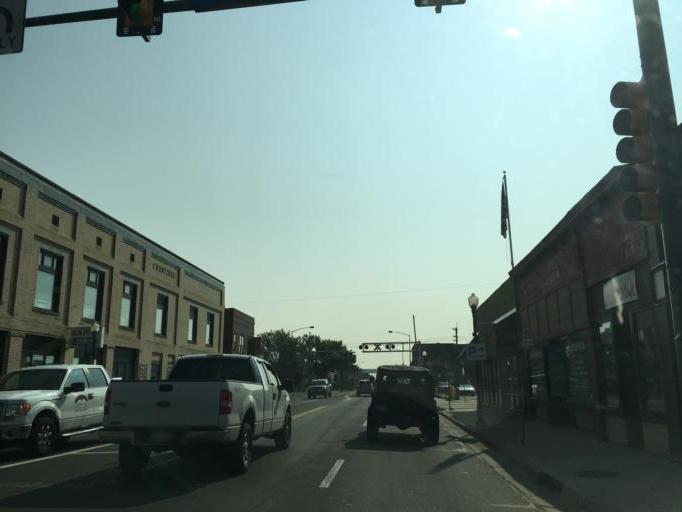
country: US
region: Colorado
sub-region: Adams County
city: Brighton
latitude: 39.9868
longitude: -104.8216
